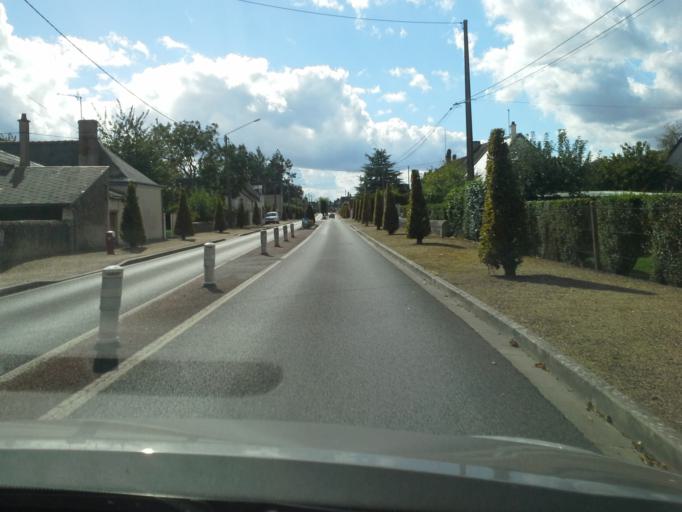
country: FR
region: Centre
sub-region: Departement du Loir-et-Cher
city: Pontlevoy
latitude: 47.3961
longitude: 1.2594
